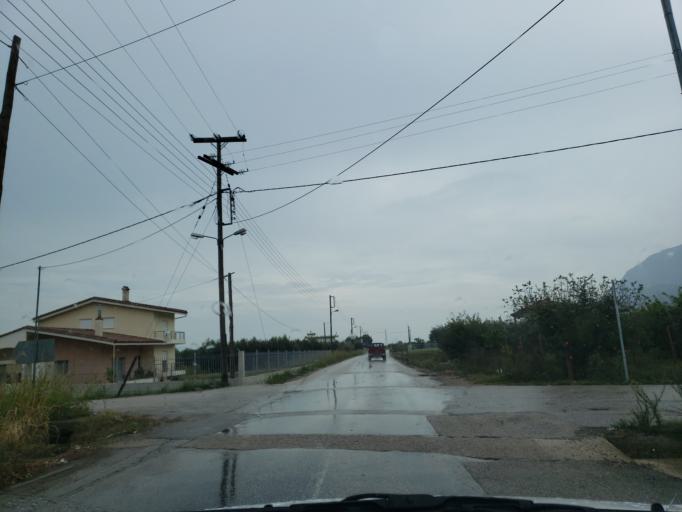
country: GR
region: Central Greece
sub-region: Nomos Fthiotidos
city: Anthili
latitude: 38.8047
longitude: 22.4480
